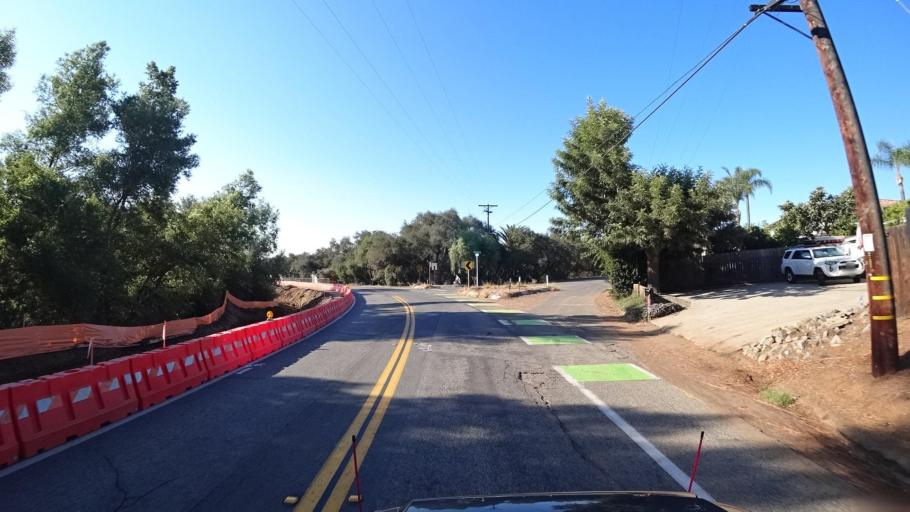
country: US
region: California
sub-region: San Diego County
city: Escondido
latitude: 33.0850
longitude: -117.0844
